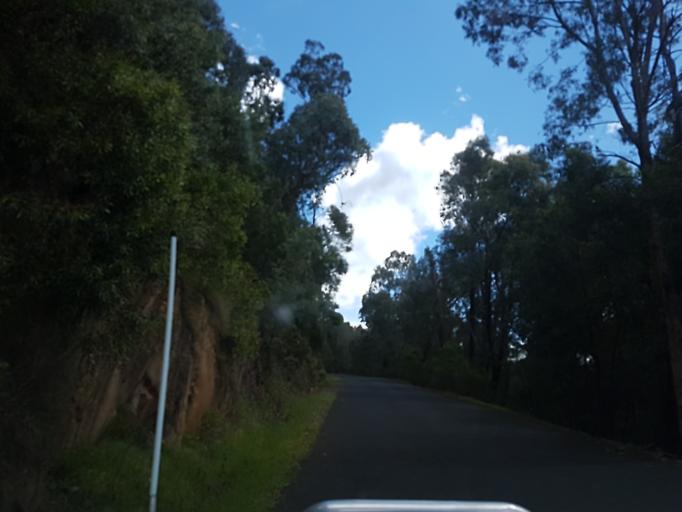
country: AU
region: Victoria
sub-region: East Gippsland
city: Bairnsdale
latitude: -37.4038
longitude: 147.2480
